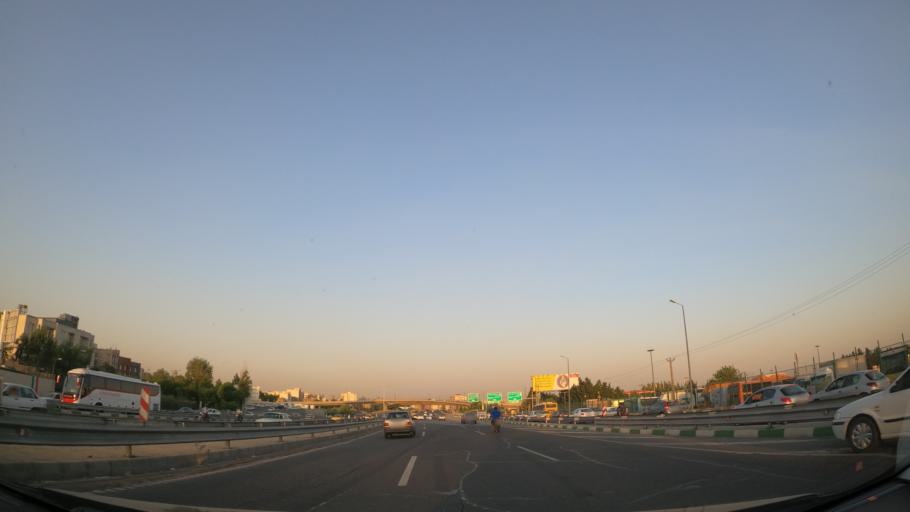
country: IR
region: Tehran
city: Tehran
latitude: 35.7131
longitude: 51.3319
